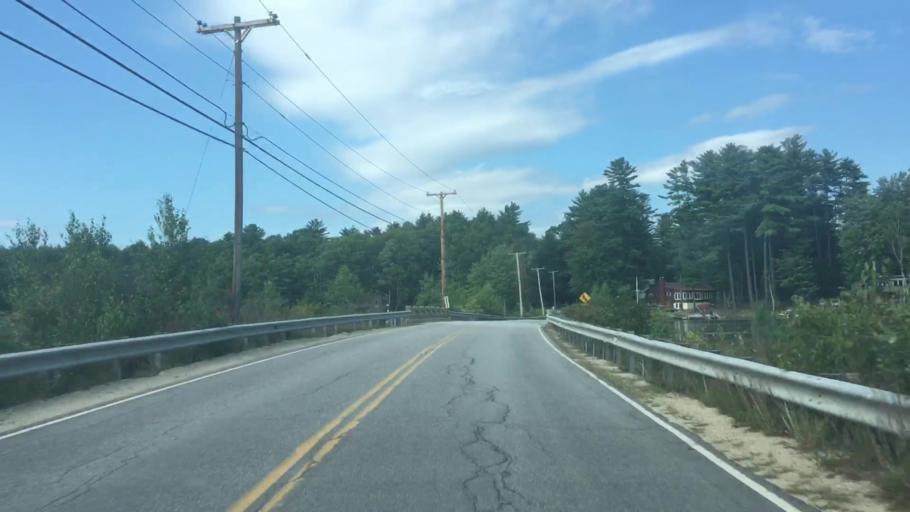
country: US
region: Maine
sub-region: Oxford County
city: Oxford
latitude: 44.1211
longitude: -70.5055
